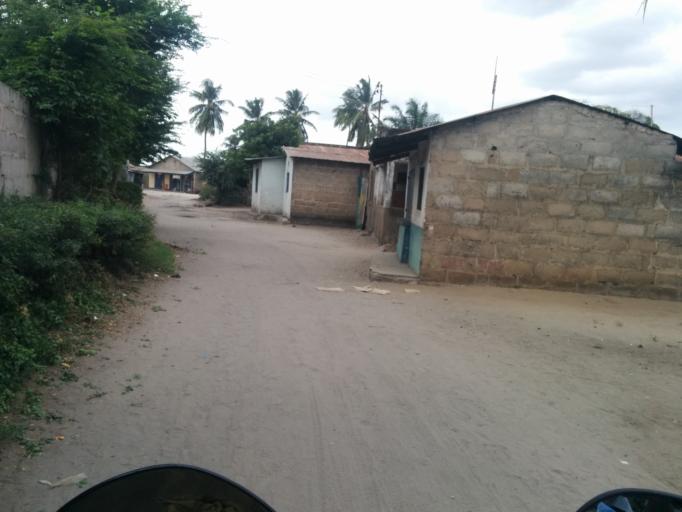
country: TZ
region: Dar es Salaam
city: Dar es Salaam
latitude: -6.8702
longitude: 39.2464
